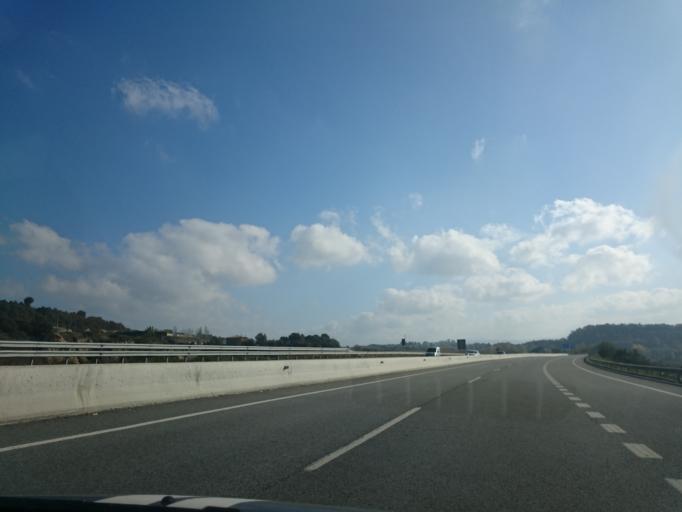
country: ES
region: Catalonia
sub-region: Provincia de Barcelona
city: Gurb
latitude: 41.9337
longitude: 2.1993
